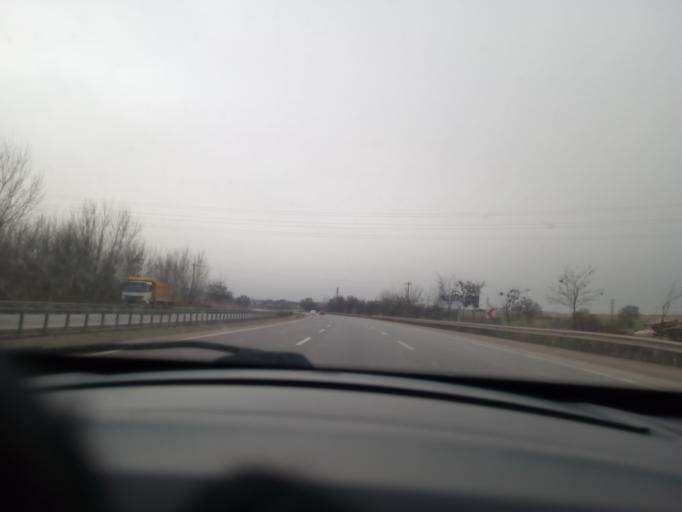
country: TR
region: Balikesir
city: Susurluk
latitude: 39.9646
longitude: 28.1704
